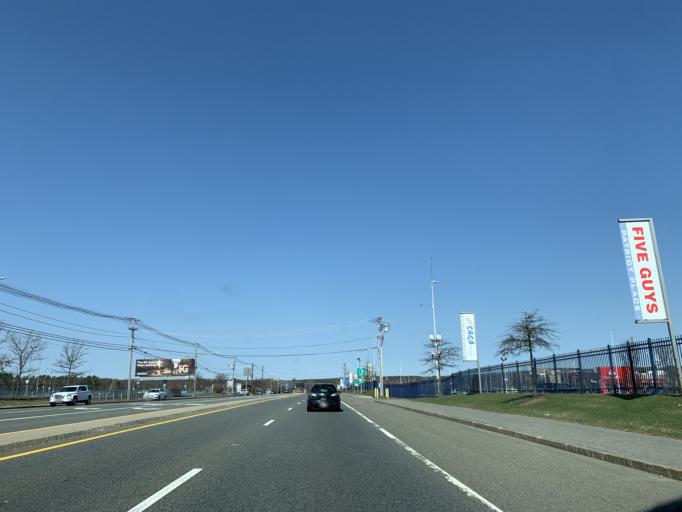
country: US
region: Massachusetts
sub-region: Norfolk County
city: Foxborough
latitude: 42.0918
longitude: -71.2699
